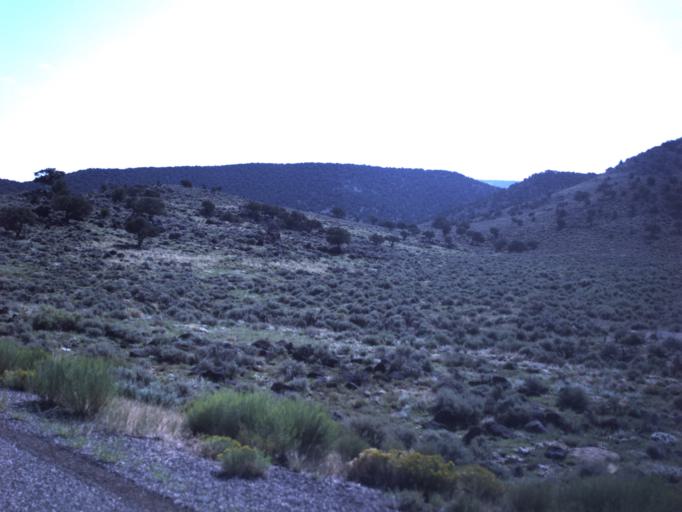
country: US
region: Utah
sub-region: Wayne County
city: Loa
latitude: 38.4701
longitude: -111.5772
